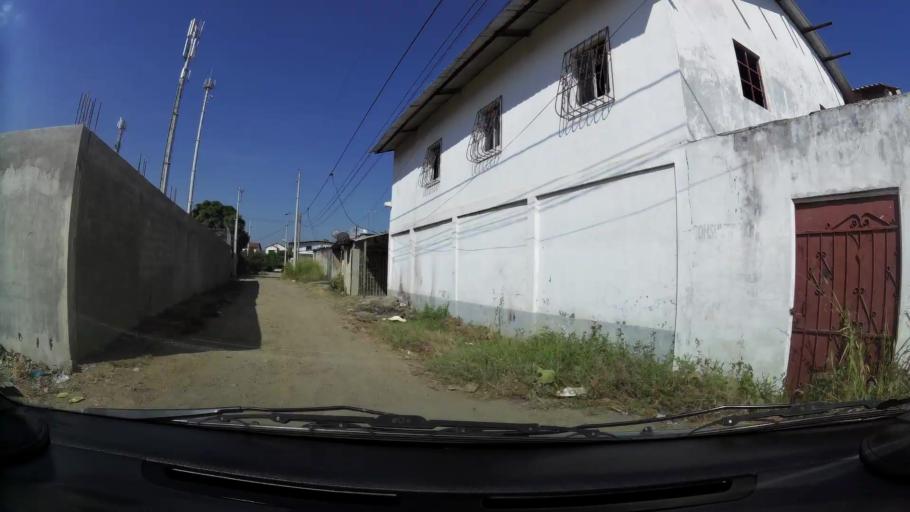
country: EC
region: Guayas
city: Santa Lucia
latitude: -2.1891
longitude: -80.0061
